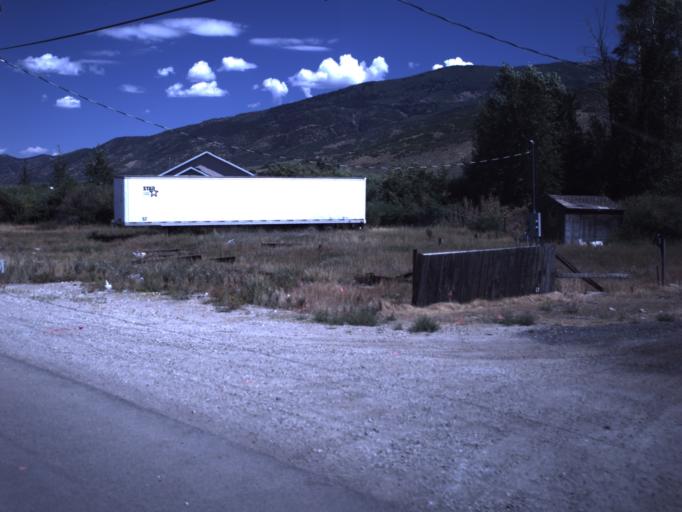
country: US
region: Utah
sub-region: Summit County
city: Kamas
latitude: 40.6515
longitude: -111.2808
